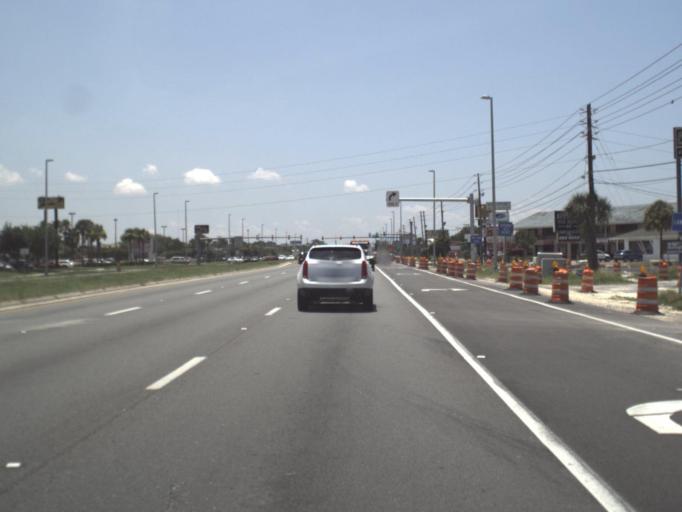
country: US
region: Florida
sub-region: Pasco County
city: Jasmine Estates
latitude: 28.2997
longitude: -82.7058
